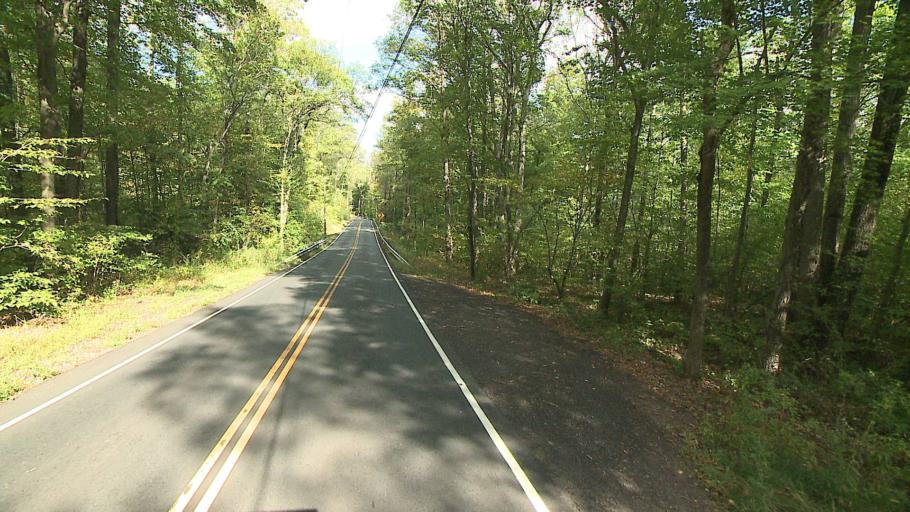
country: US
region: Connecticut
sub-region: New Haven County
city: Prospect
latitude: 41.4693
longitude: -72.9467
